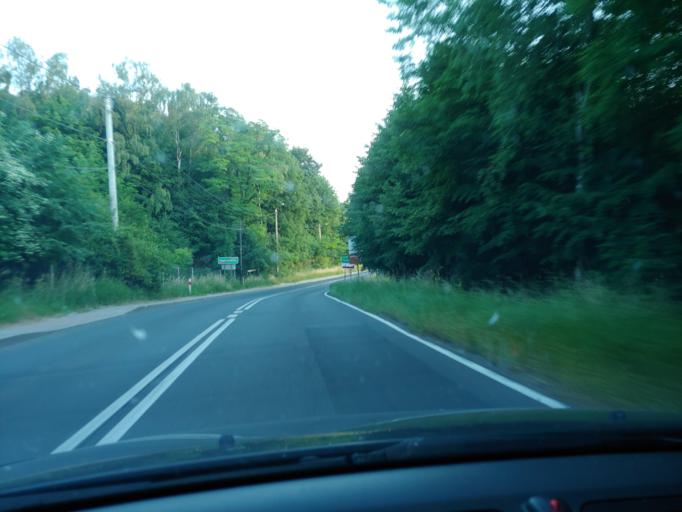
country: PL
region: Lesser Poland Voivodeship
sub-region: Powiat chrzanowski
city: Myslachowice
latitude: 50.1786
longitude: 19.4749
